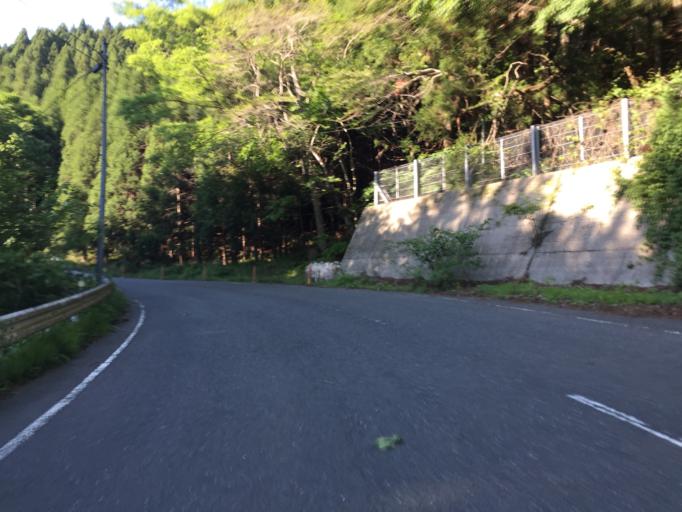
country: JP
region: Ibaraki
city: Kitaibaraki
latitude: 36.8729
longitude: 140.6344
